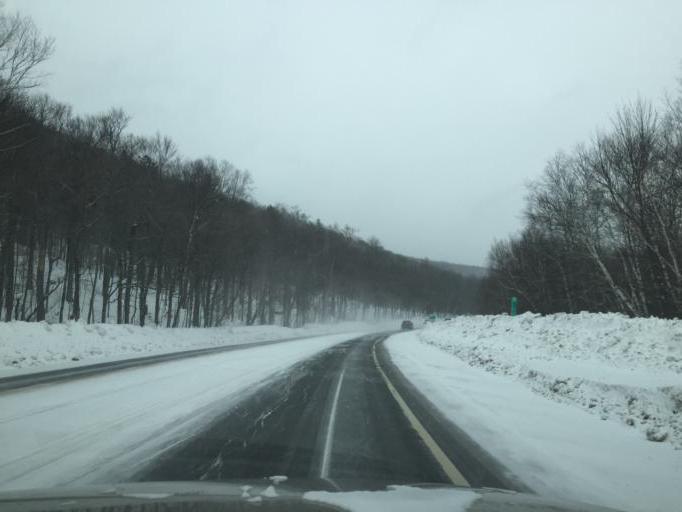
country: US
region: New Hampshire
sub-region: Coos County
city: Gorham
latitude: 44.2330
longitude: -71.2569
